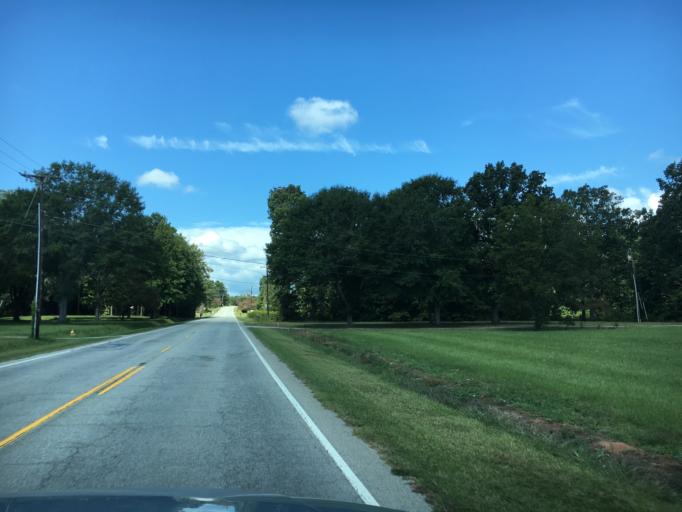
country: US
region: South Carolina
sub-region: Greenville County
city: Tigerville
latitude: 35.0131
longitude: -82.3752
